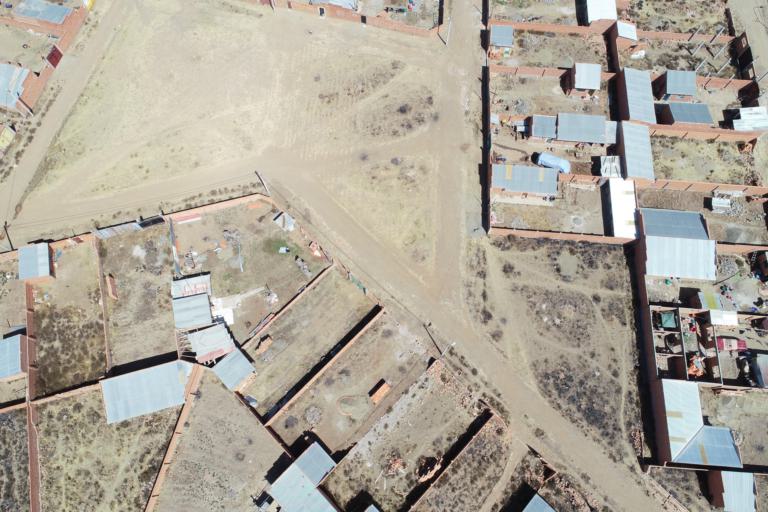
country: BO
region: La Paz
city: La Paz
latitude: -16.5926
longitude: -68.2138
